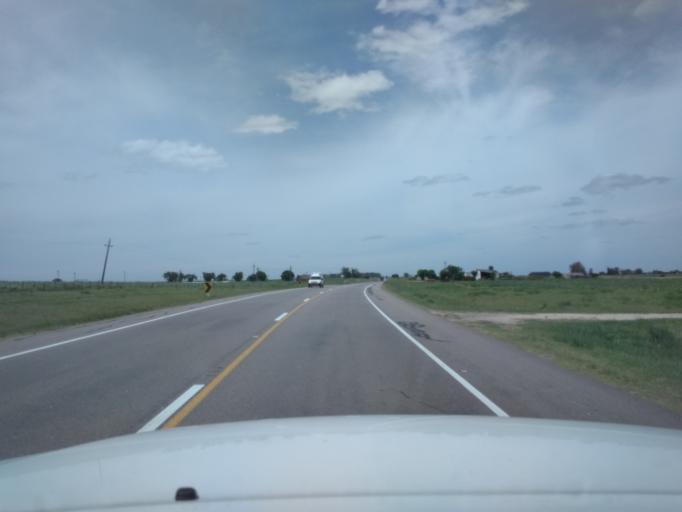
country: UY
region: Florida
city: Cardal
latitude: -34.3167
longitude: -56.2416
